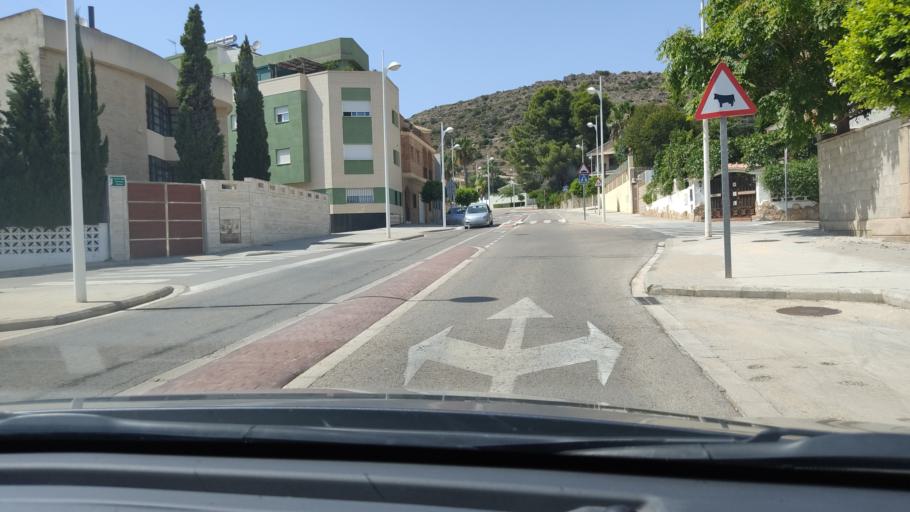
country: ES
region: Valencia
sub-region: Provincia de Valencia
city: Monserrat
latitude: 39.3596
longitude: -0.5990
